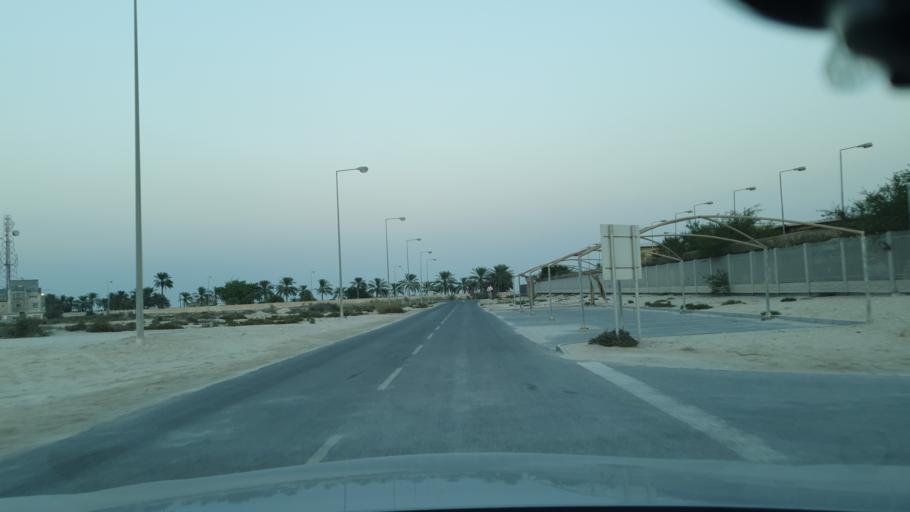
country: BH
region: Central Governorate
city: Dar Kulayb
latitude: 25.9766
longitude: 50.6126
